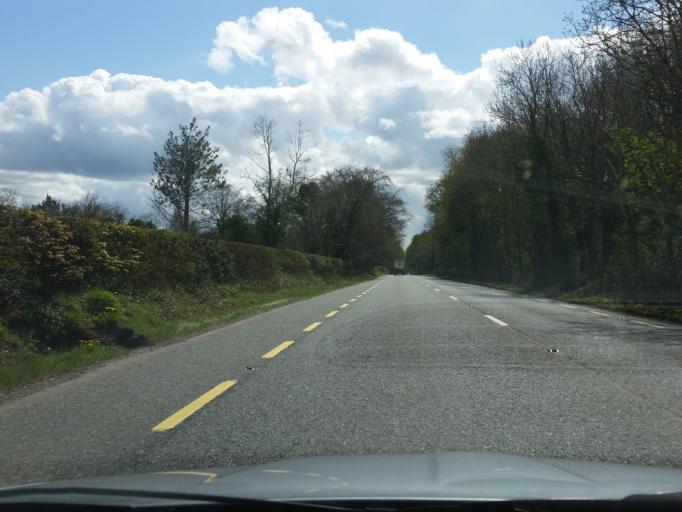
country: IE
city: Kentstown
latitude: 53.6316
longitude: -6.4926
